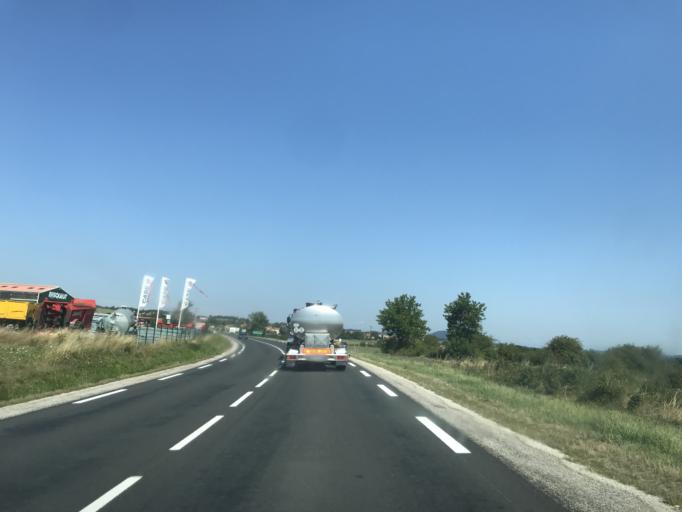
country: FR
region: Auvergne
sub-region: Departement de la Haute-Loire
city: Saint-Paulien
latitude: 45.1065
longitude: 3.7489
